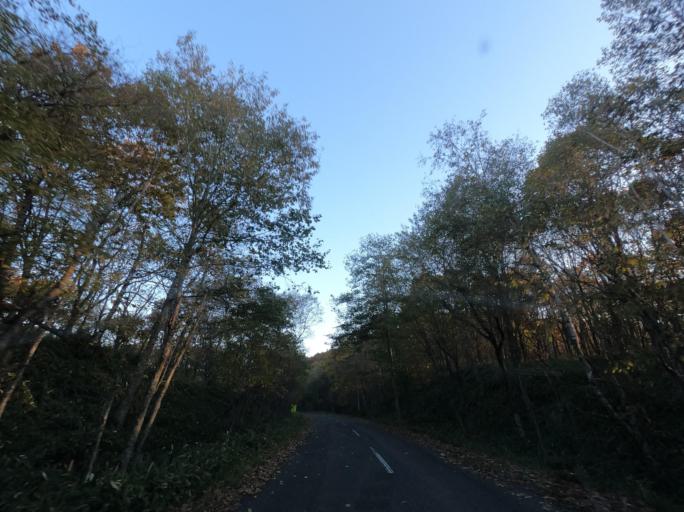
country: JP
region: Hokkaido
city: Kushiro
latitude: 43.2064
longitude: 144.4551
